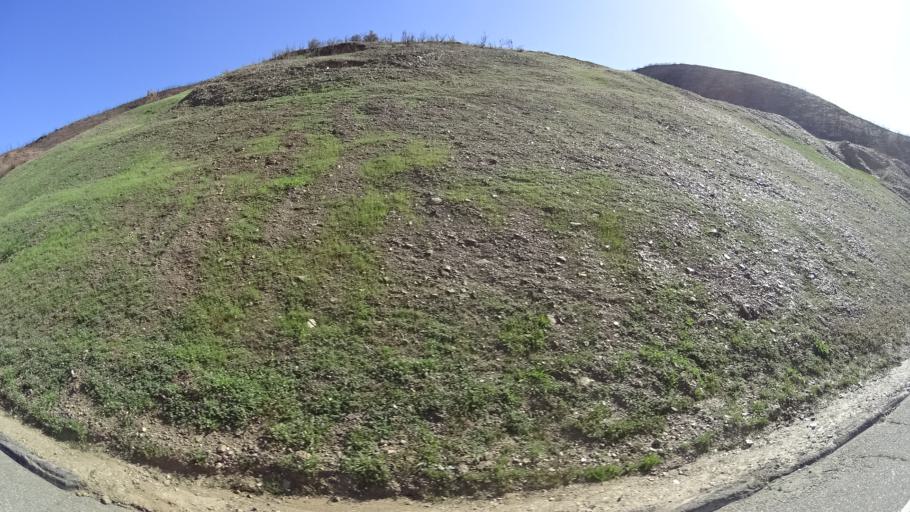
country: US
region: California
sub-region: Tehama County
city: Rancho Tehama Reserve
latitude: 39.6536
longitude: -122.6190
